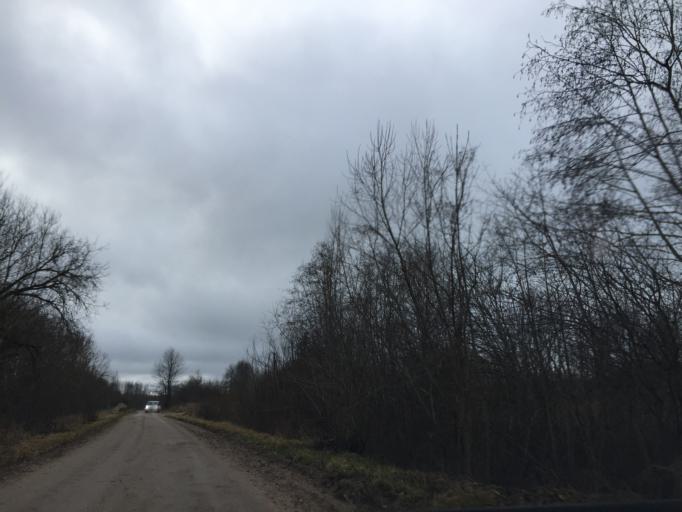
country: LV
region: Broceni
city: Broceni
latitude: 56.6678
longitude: 22.5537
